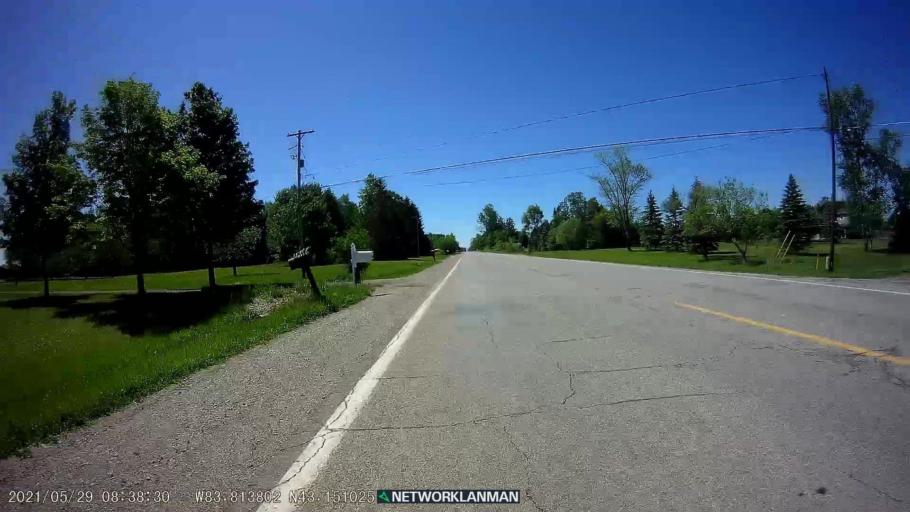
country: US
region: Michigan
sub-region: Genesee County
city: Montrose
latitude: 43.1512
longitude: -83.8138
